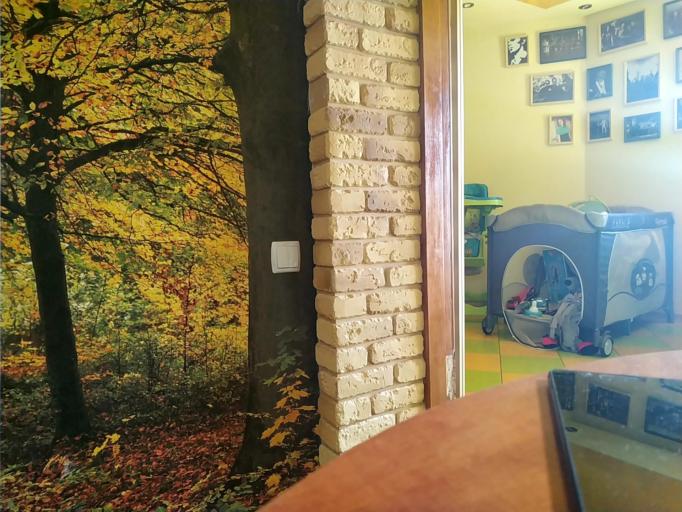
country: RU
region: Tverskaya
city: Vyshniy Volochek
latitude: 57.5890
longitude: 34.5591
